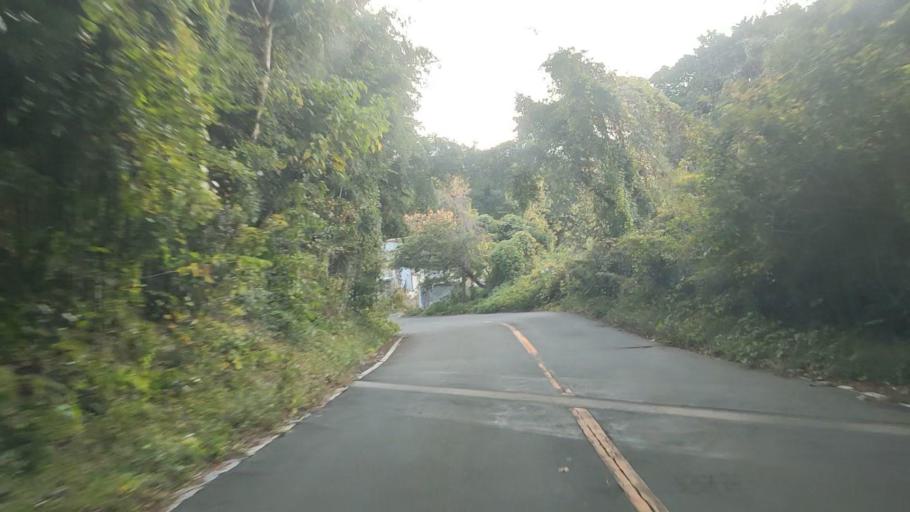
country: JP
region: Shizuoka
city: Mishima
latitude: 35.1533
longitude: 138.9297
